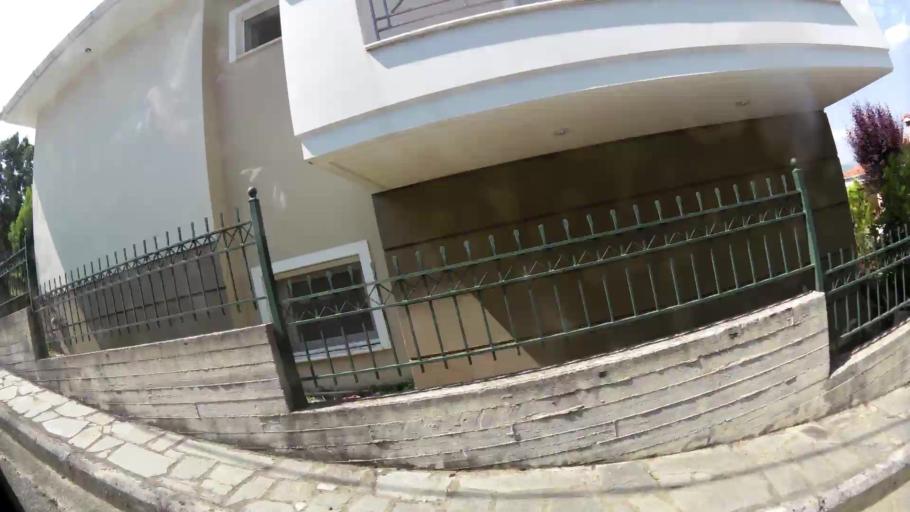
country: GR
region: West Macedonia
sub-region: Nomos Kozanis
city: Koila
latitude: 40.3263
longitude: 21.7937
